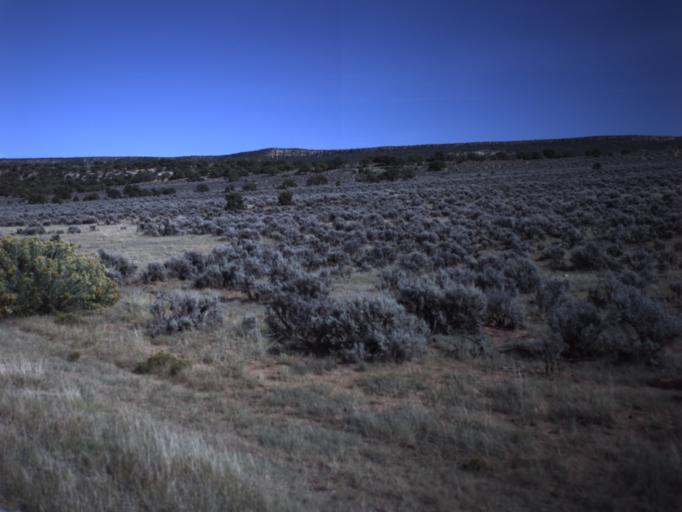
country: US
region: Utah
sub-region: San Juan County
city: Monticello
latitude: 37.9971
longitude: -109.4753
